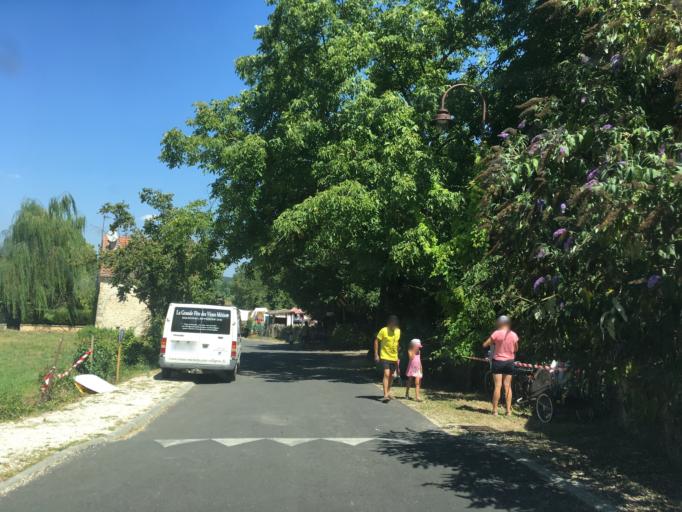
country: FR
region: Aquitaine
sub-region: Departement de la Dordogne
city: Eyvigues-et-Eybenes
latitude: 44.9740
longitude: 1.3274
